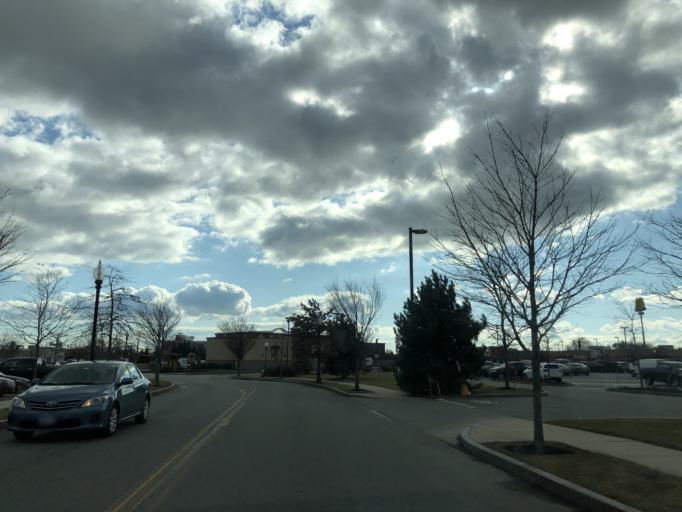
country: US
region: Massachusetts
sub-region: Bristol County
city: Acushnet
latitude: 41.6581
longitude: -70.9204
